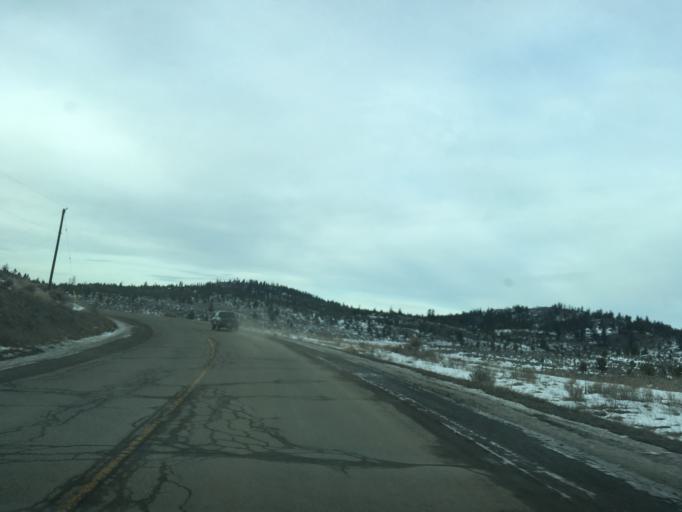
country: CA
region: British Columbia
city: Kamloops
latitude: 50.6285
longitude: -120.4413
